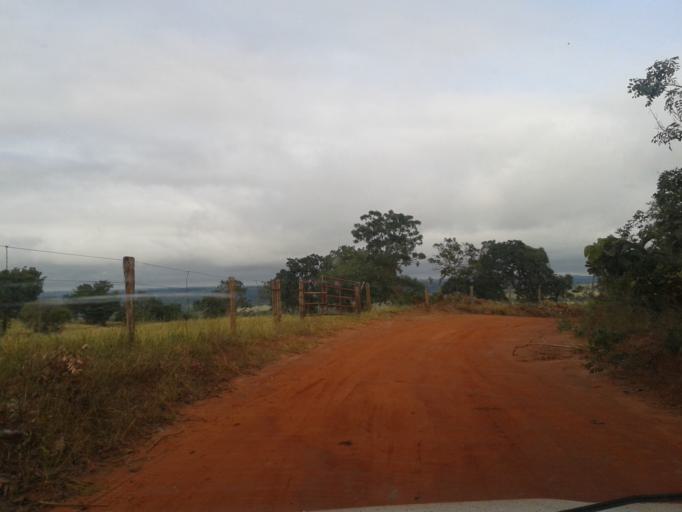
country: BR
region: Minas Gerais
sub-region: Campina Verde
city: Campina Verde
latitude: -19.4031
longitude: -49.6277
